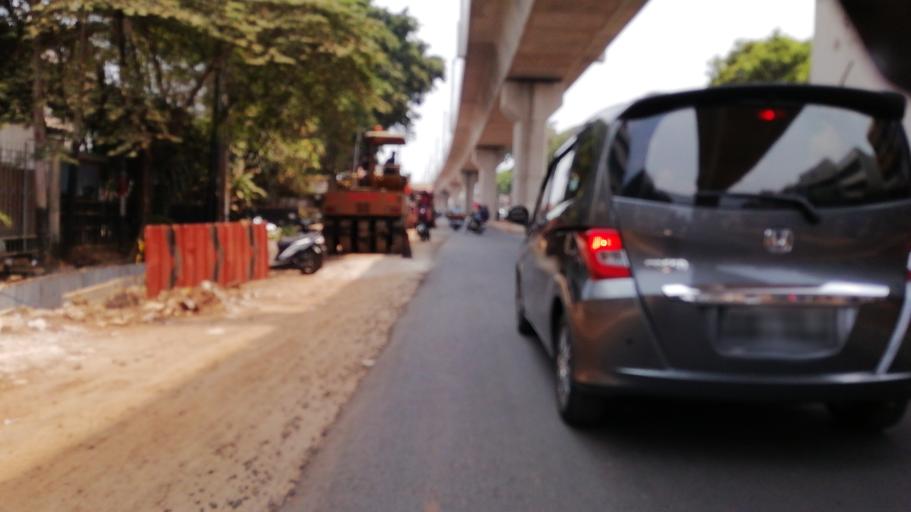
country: ID
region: Banten
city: South Tangerang
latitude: -6.2860
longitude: 106.7957
